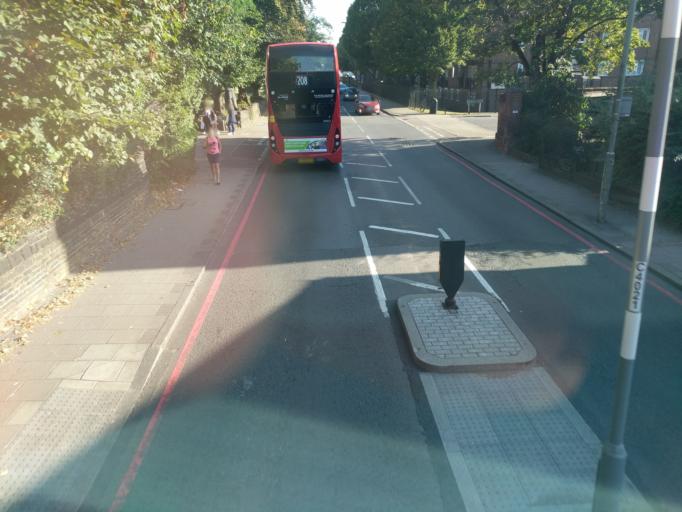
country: GB
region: England
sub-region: Greater London
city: Bromley
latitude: 51.4124
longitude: 0.0087
